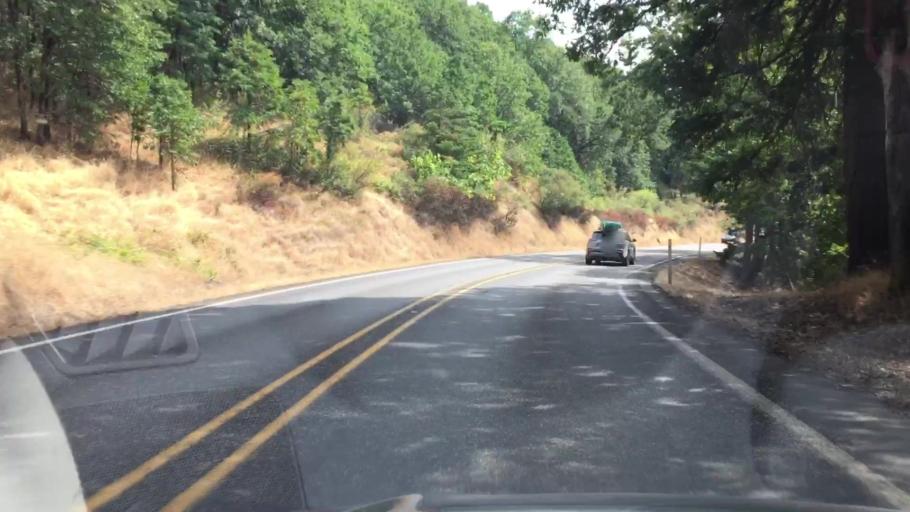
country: US
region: Washington
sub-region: Klickitat County
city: White Salmon
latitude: 45.7550
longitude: -121.5179
